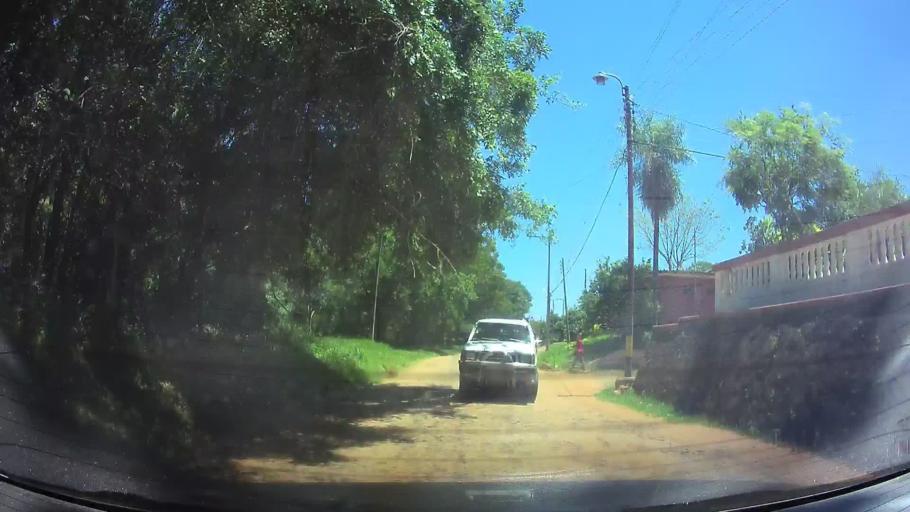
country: PY
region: Central
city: Limpio
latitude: -25.2472
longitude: -57.4856
